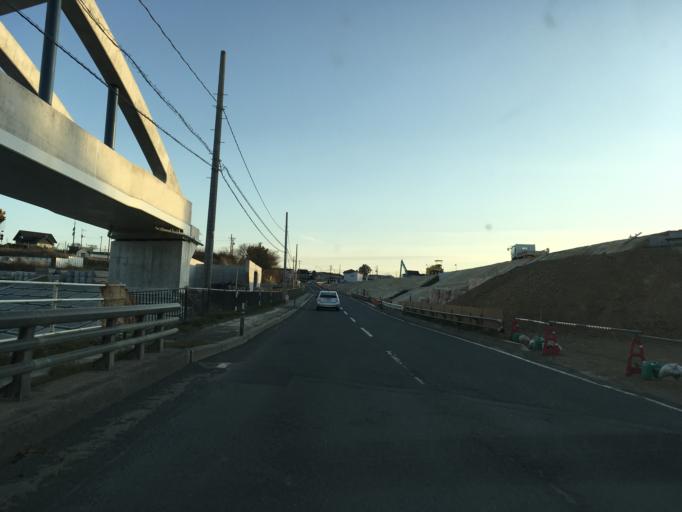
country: JP
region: Iwate
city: Ofunato
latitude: 38.8243
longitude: 141.5750
